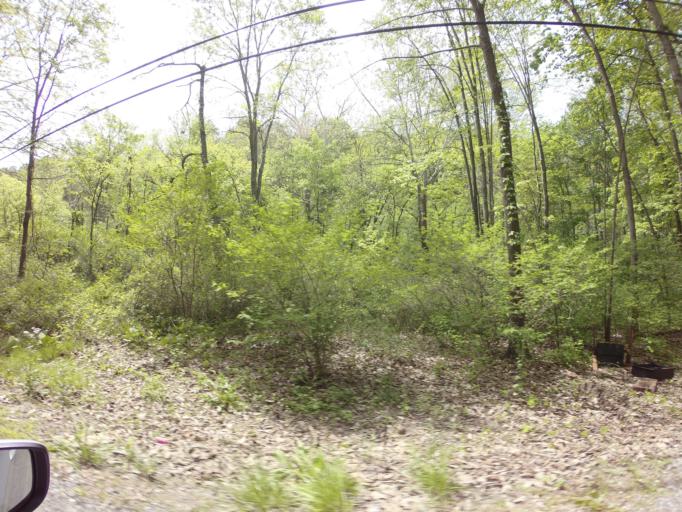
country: US
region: Maryland
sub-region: Carroll County
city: New Windsor
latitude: 39.4917
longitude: -77.0972
